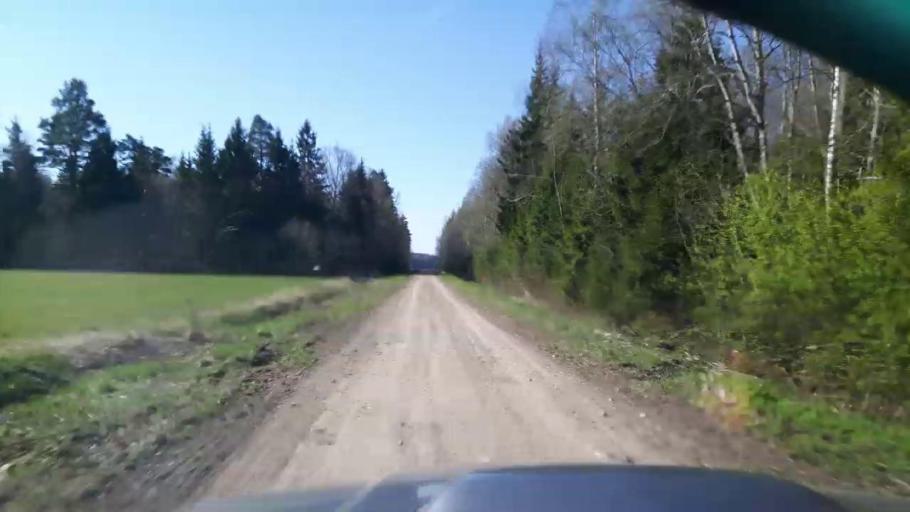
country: EE
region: Paernumaa
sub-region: Tootsi vald
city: Tootsi
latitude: 58.5158
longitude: 24.9282
